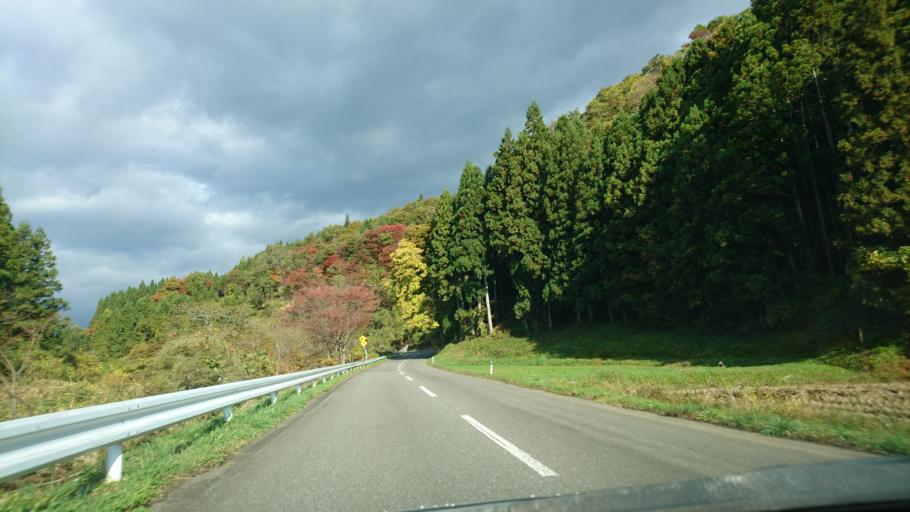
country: JP
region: Iwate
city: Mizusawa
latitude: 39.0827
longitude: 140.9977
